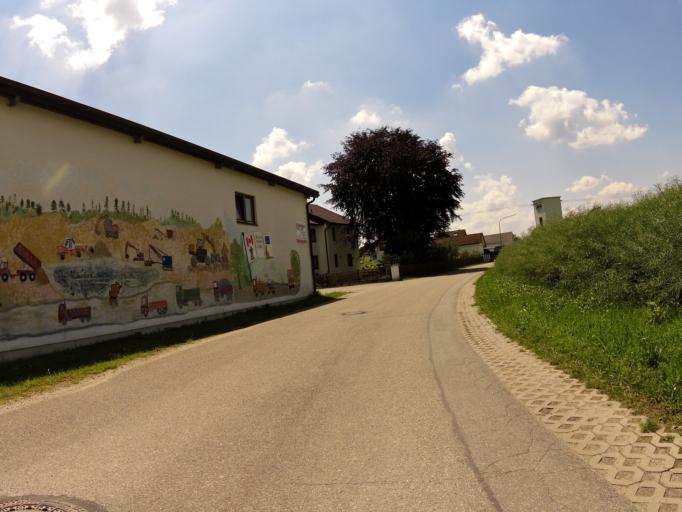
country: DE
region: Bavaria
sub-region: Lower Bavaria
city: Bruckberg
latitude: 48.5120
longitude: 12.0179
